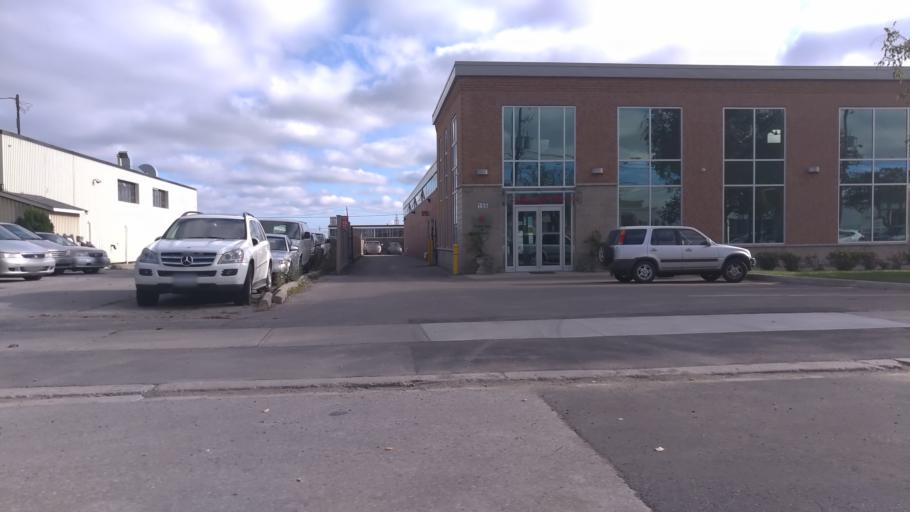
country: CA
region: Ontario
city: Toronto
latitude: 43.7199
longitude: -79.4669
